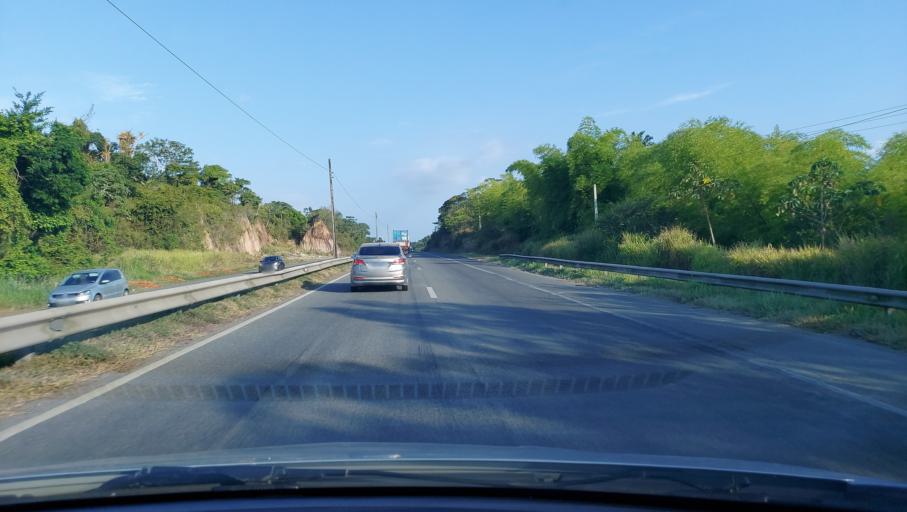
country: BR
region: Bahia
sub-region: Conceicao Do Jacuipe
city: Conceicao do Jacuipe
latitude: -12.3927
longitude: -38.7788
